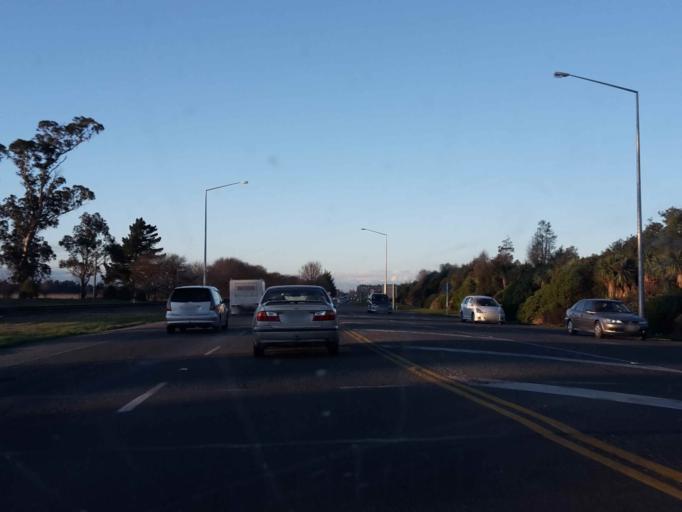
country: NZ
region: Canterbury
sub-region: Selwyn District
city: Rolleston
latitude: -43.5879
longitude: 172.3865
